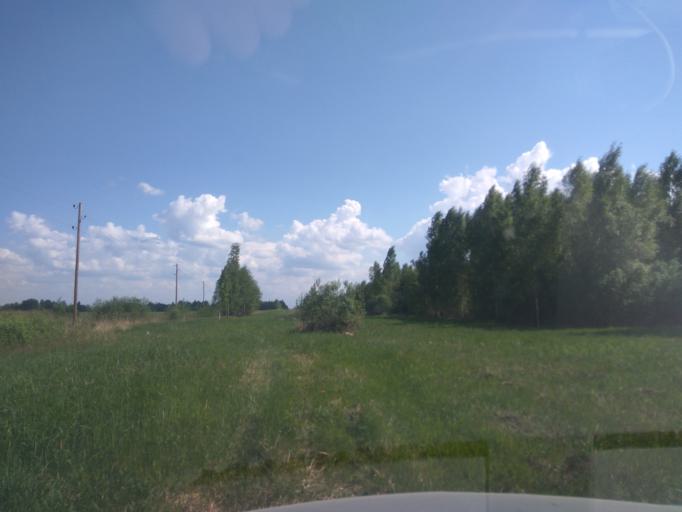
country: LV
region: Kuldigas Rajons
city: Kuldiga
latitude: 57.1792
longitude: 22.0061
